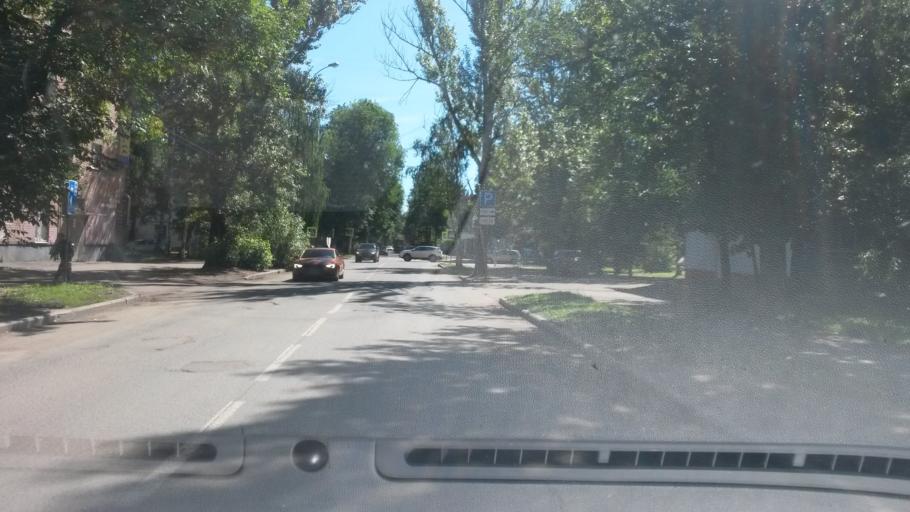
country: RU
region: Jaroslavl
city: Yaroslavl
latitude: 57.6311
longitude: 39.8631
